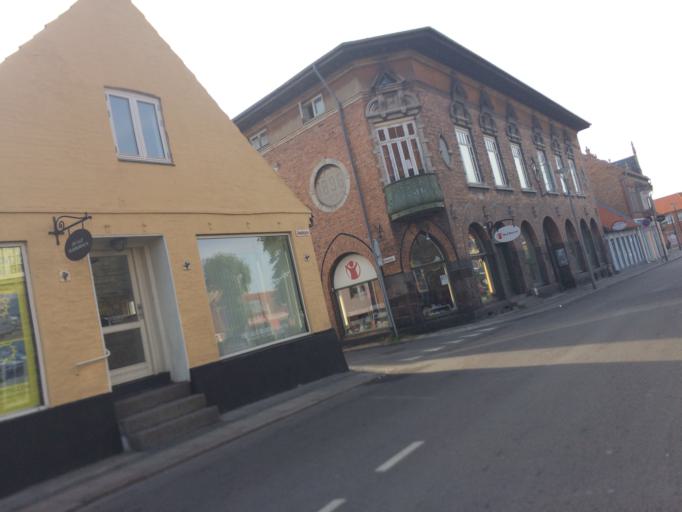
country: DK
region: Capital Region
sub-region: Bornholm Kommune
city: Ronne
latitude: 55.1002
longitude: 14.7009
